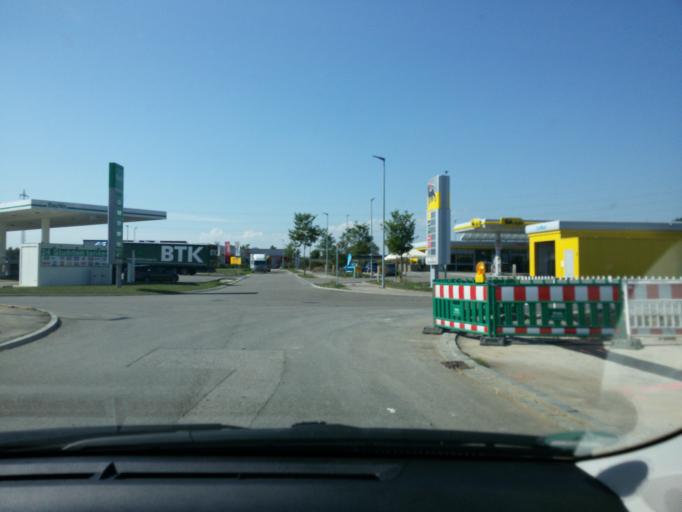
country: DE
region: Bavaria
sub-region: Swabia
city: Noerdlingen
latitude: 48.8644
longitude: 10.5193
